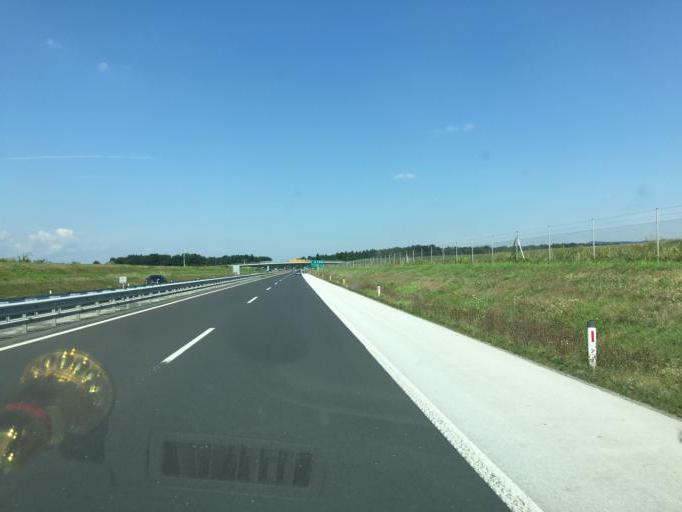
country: SI
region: Kidricevo
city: Kidricevo
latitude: 46.4230
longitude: 15.7999
